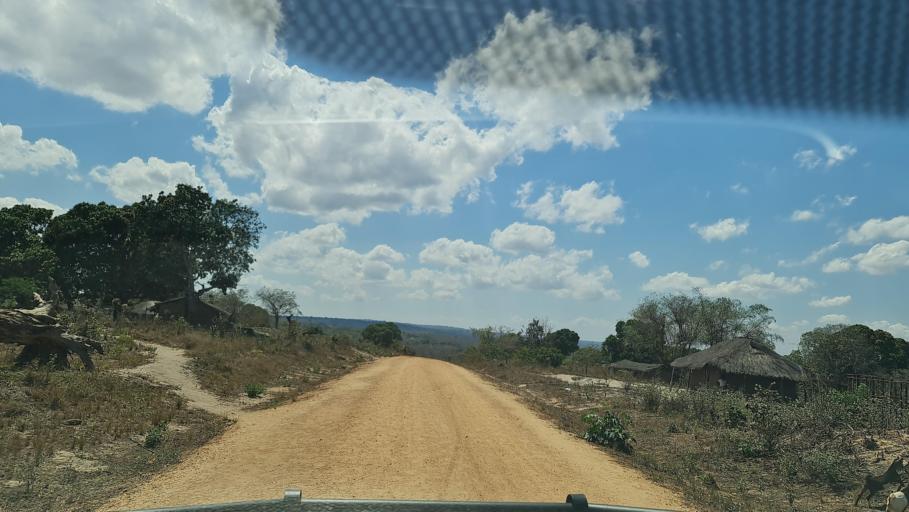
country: MZ
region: Nampula
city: Nacala
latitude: -14.1755
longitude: 40.2140
